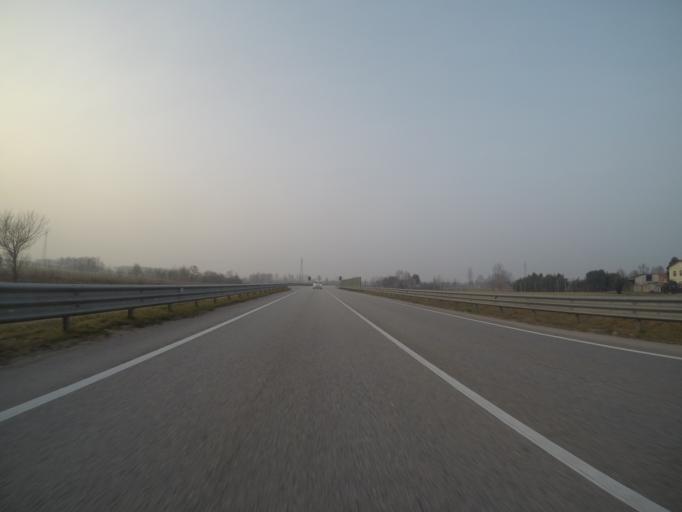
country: IT
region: Veneto
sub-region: Provincia di Treviso
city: Resana
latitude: 45.6380
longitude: 11.9310
